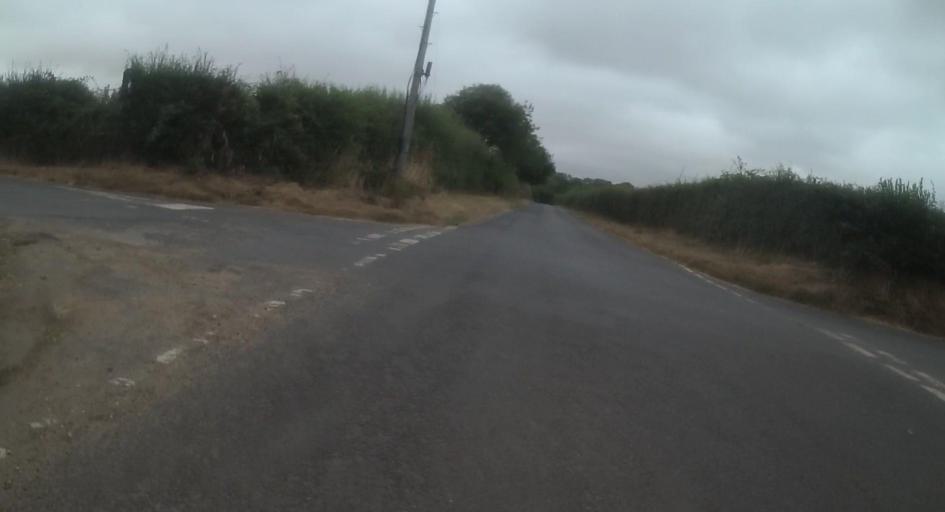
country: GB
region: England
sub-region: Dorset
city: Bovington Camp
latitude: 50.7348
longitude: -2.2108
